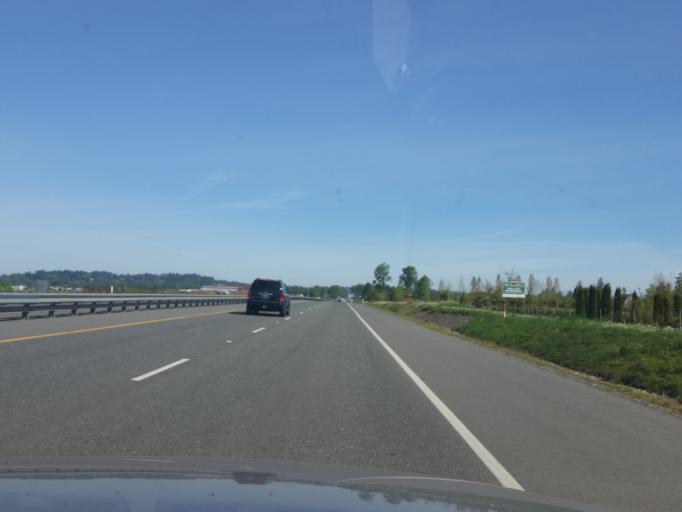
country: US
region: Washington
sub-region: Snohomish County
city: Snohomish
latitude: 47.8907
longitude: -122.1095
